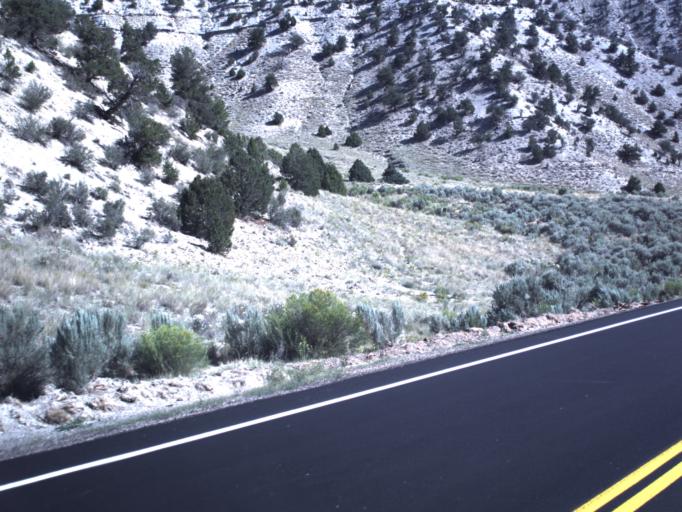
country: US
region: Utah
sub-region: Duchesne County
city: Duchesne
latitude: 39.9573
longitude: -110.6480
